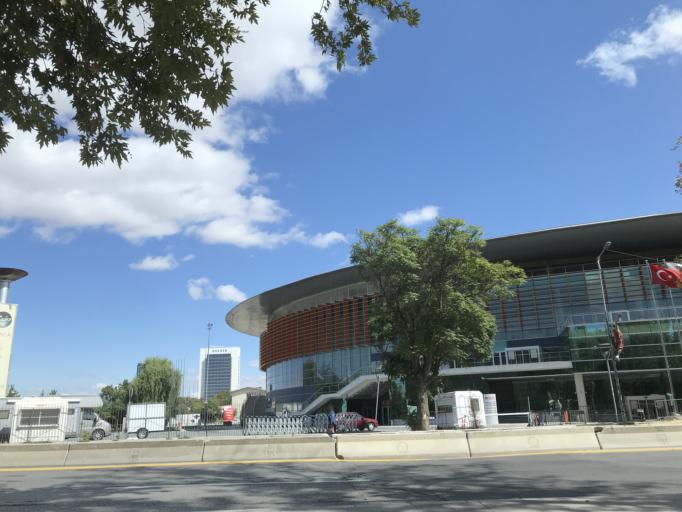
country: TR
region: Ankara
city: Ankara
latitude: 39.9375
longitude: 32.8426
